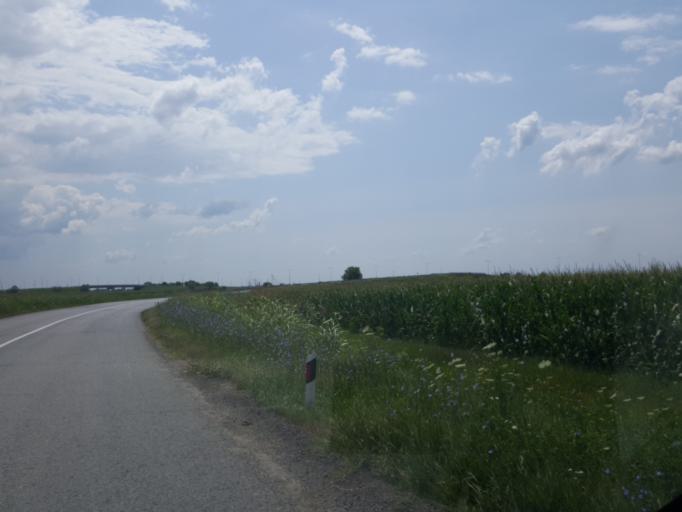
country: RS
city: Ravnje
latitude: 45.0432
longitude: 19.3798
